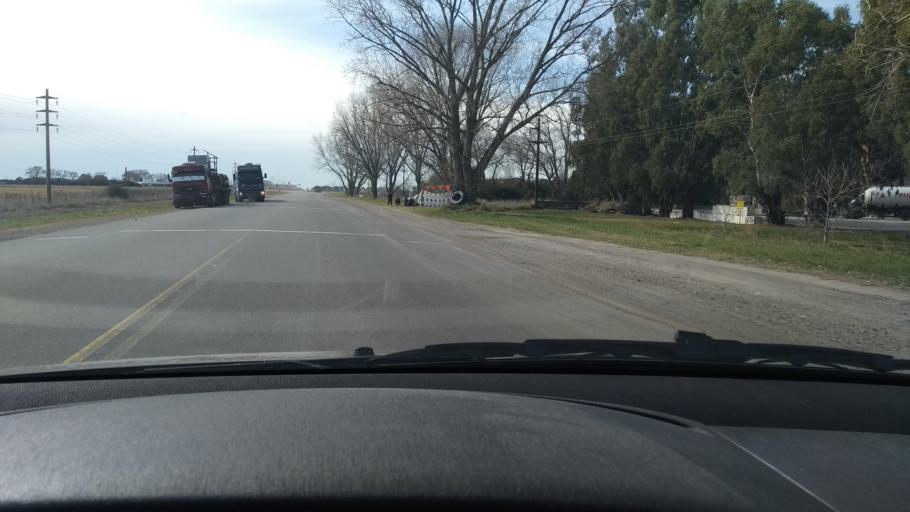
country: AR
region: Buenos Aires
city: Olavarria
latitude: -36.9404
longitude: -60.2346
